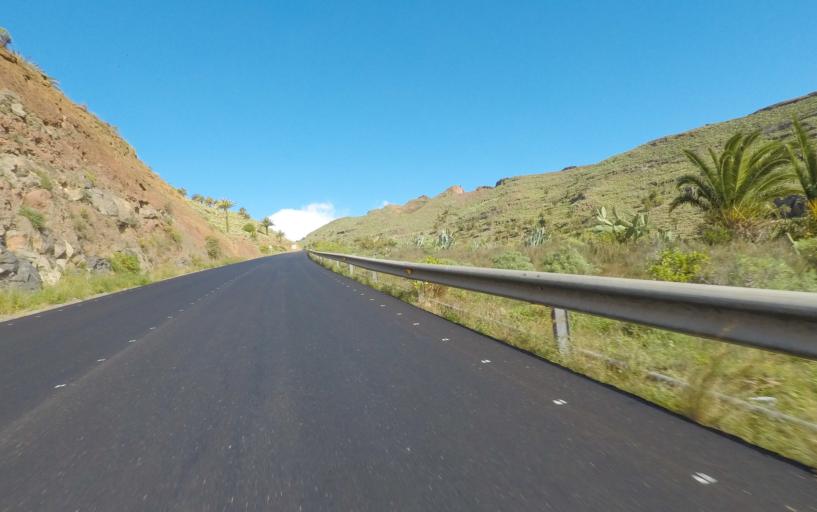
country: ES
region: Canary Islands
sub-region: Provincia de Santa Cruz de Tenerife
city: Alajero
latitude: 28.0706
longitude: -17.2070
